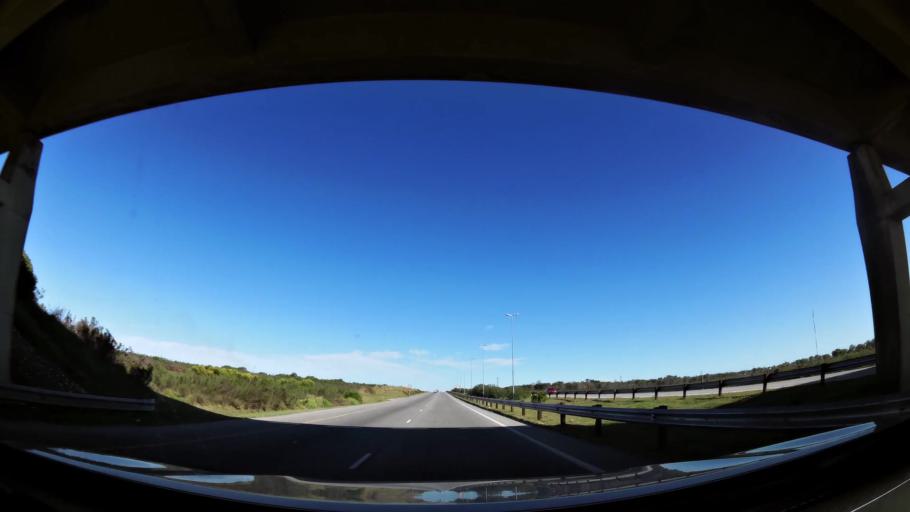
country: ZA
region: Eastern Cape
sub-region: Nelson Mandela Bay Metropolitan Municipality
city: Port Elizabeth
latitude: -33.9480
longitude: 25.4562
